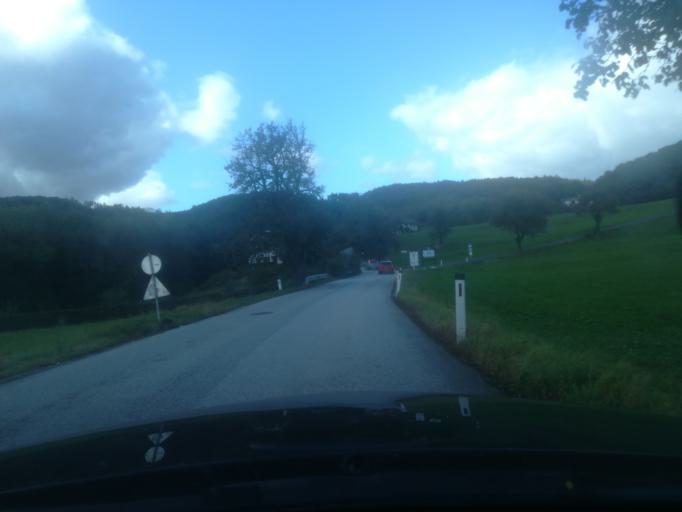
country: AT
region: Upper Austria
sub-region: Linz Stadt
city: Linz
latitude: 48.3366
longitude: 14.2758
